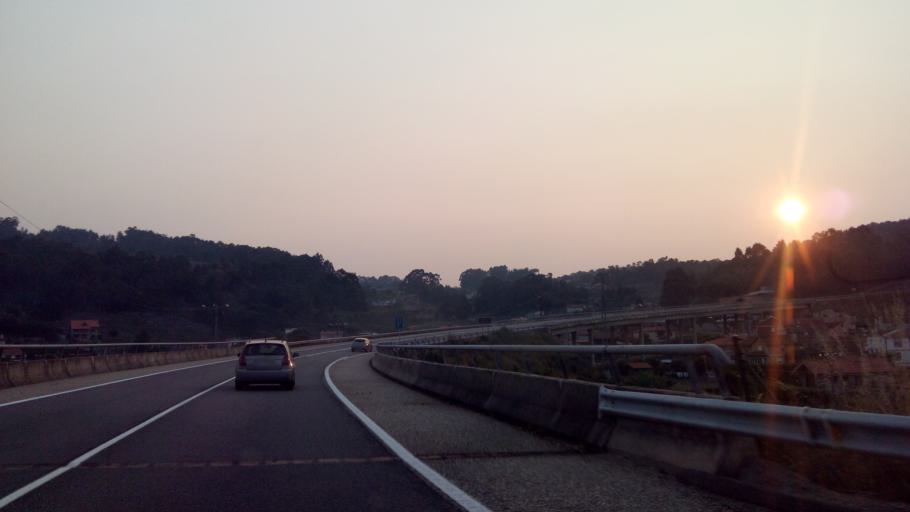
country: ES
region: Galicia
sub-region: Provincia de Pontevedra
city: Baiona
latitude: 42.1080
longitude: -8.8424
